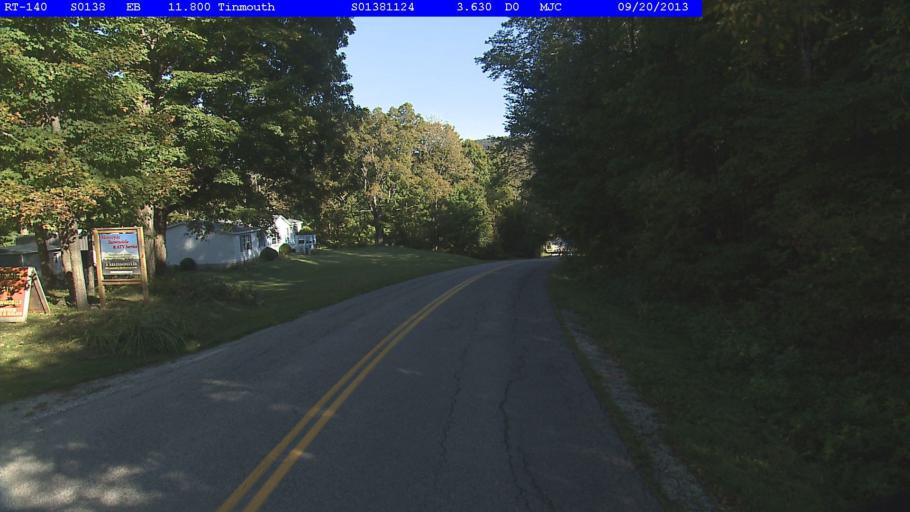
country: US
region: Vermont
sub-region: Rutland County
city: West Rutland
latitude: 43.4508
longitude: -73.0442
